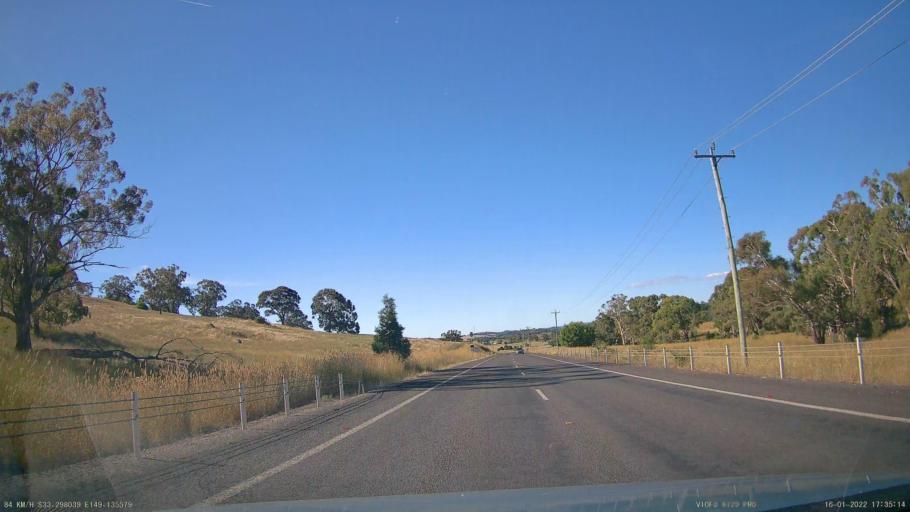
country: AU
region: New South Wales
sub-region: Orange Municipality
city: Orange
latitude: -33.2978
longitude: 149.1355
